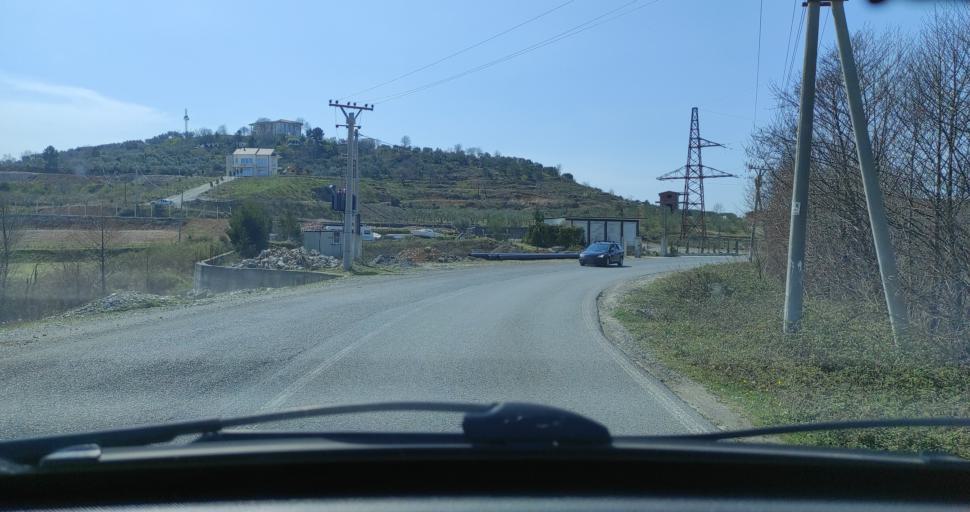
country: AL
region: Shkoder
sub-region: Rrethi i Shkodres
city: Vau i Dejes
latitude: 42.0022
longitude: 19.6307
